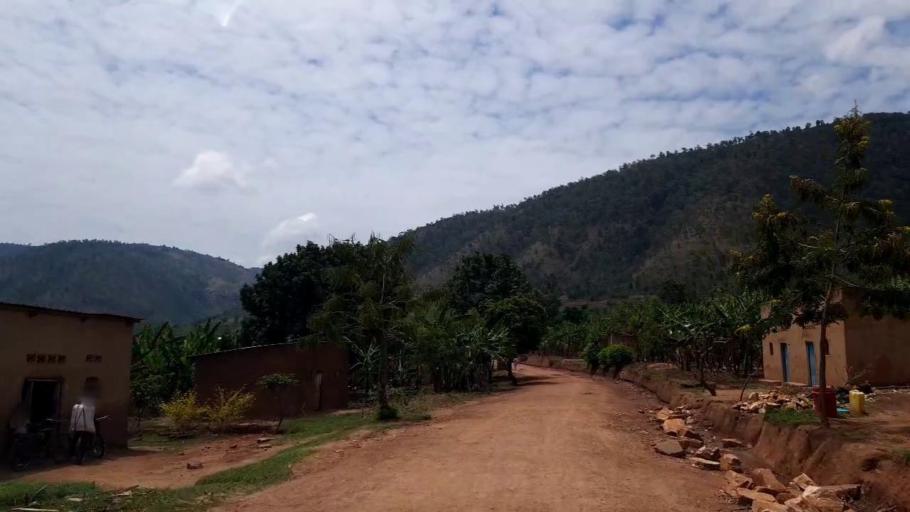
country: RW
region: Northern Province
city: Byumba
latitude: -1.4985
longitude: 30.1941
